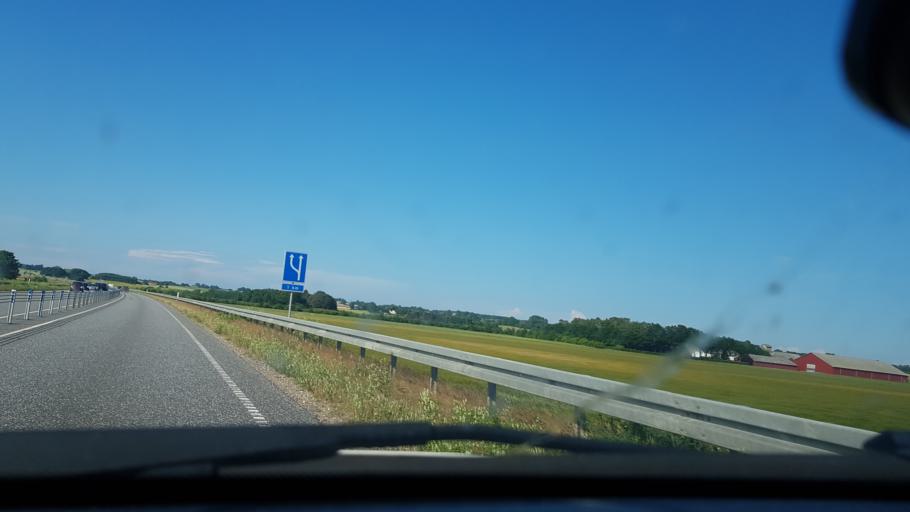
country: DK
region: Zealand
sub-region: Odsherred Kommune
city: Hojby
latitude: 55.8369
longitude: 11.5989
